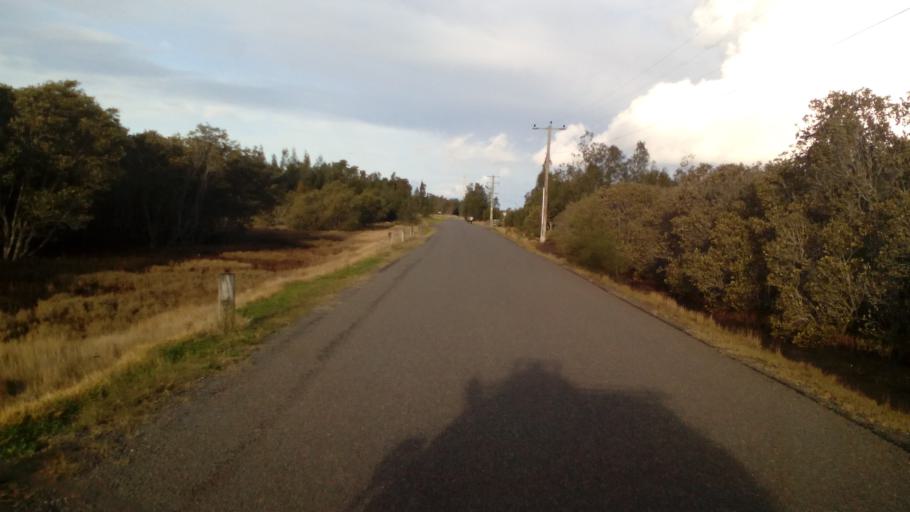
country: AU
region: New South Wales
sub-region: Newcastle
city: Mayfield West
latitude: -32.8449
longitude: 151.6988
